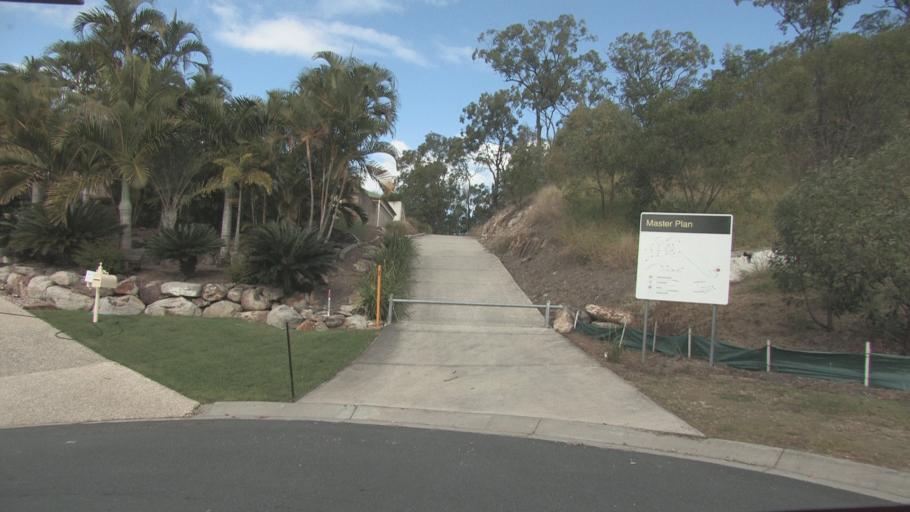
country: AU
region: Queensland
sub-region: Logan
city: Windaroo
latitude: -27.7305
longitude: 153.2015
